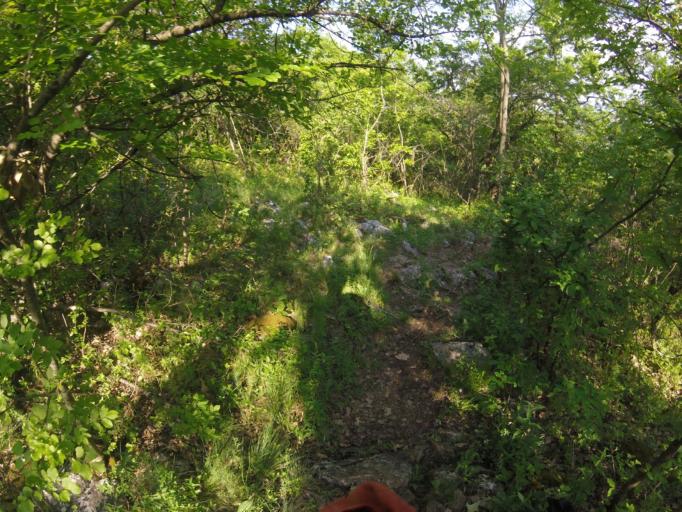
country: SK
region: Kosicky
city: Medzev
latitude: 48.6179
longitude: 20.8561
